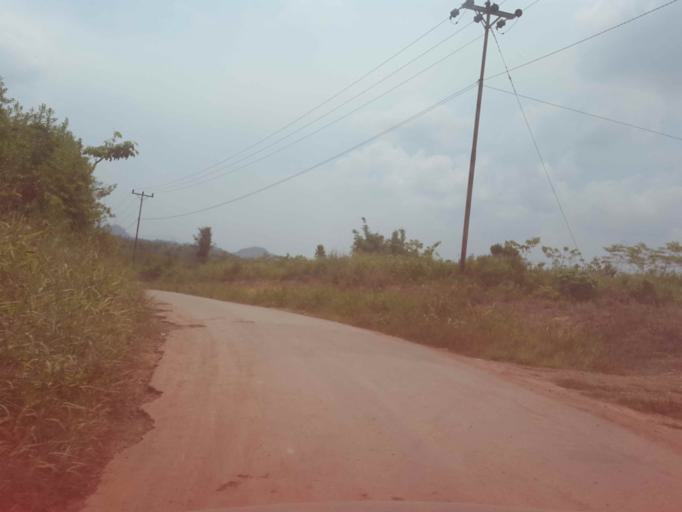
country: MY
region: Sarawak
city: Simanggang
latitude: 1.0159
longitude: 111.8850
